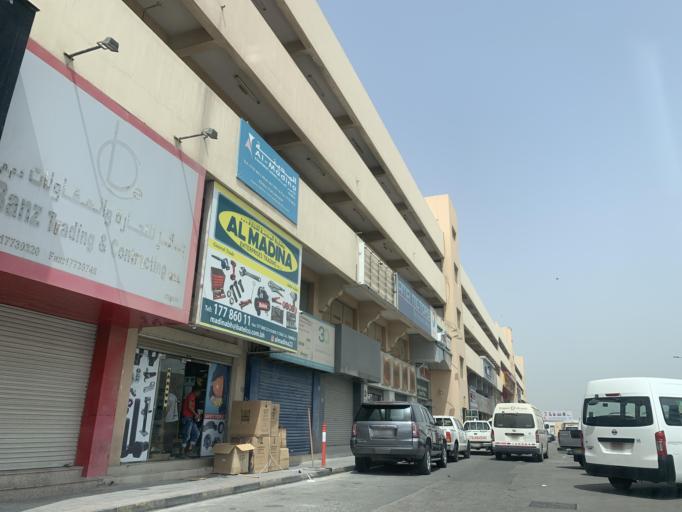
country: BH
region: Northern
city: Madinat `Isa
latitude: 26.1865
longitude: 50.5296
